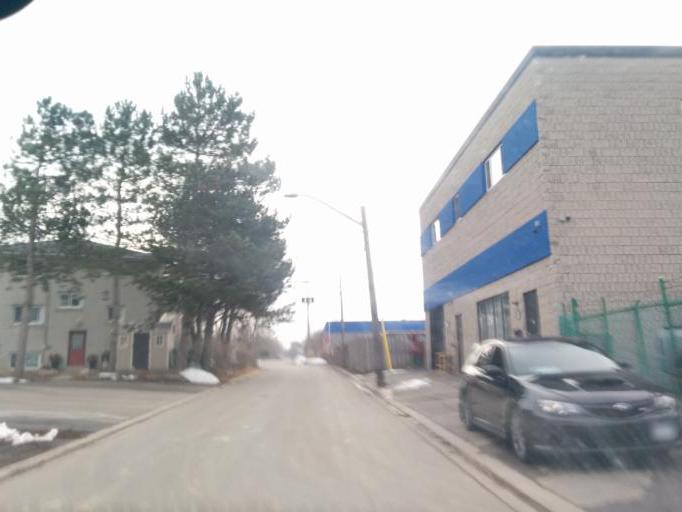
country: CA
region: Ontario
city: Mississauga
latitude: 43.5462
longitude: -79.5971
